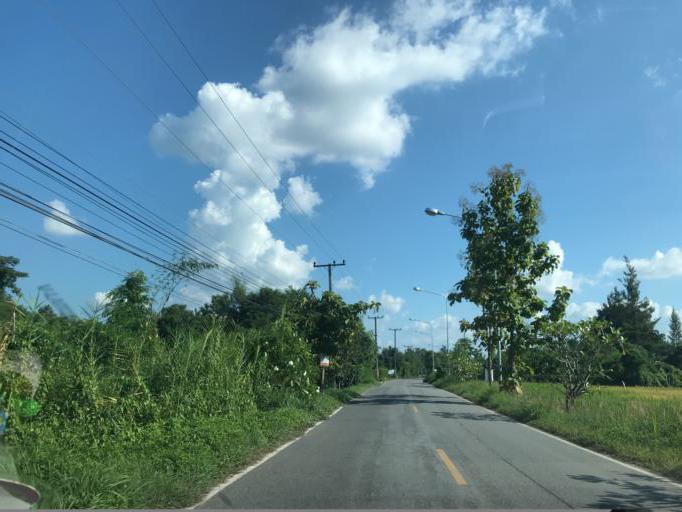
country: TH
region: Chiang Mai
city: Doi Lo
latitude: 18.5347
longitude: 98.8415
